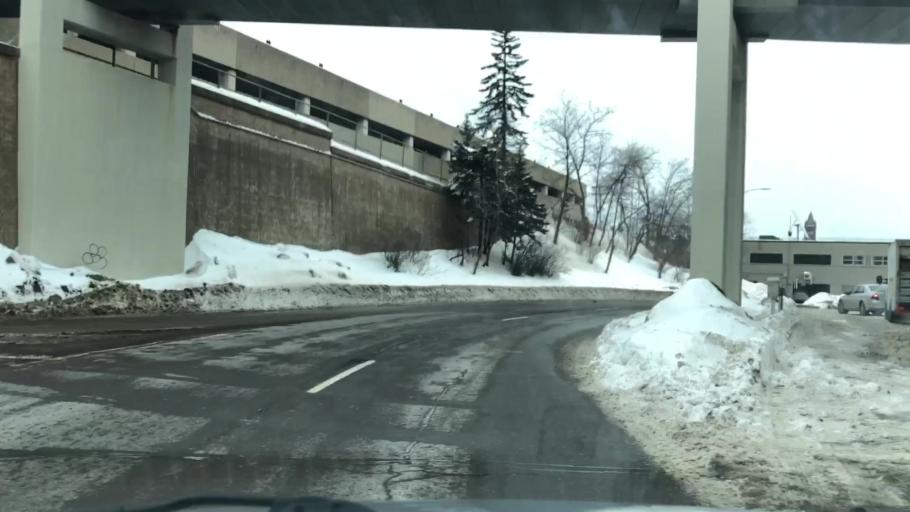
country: US
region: Minnesota
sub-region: Saint Louis County
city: Duluth
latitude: 46.7836
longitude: -92.1072
